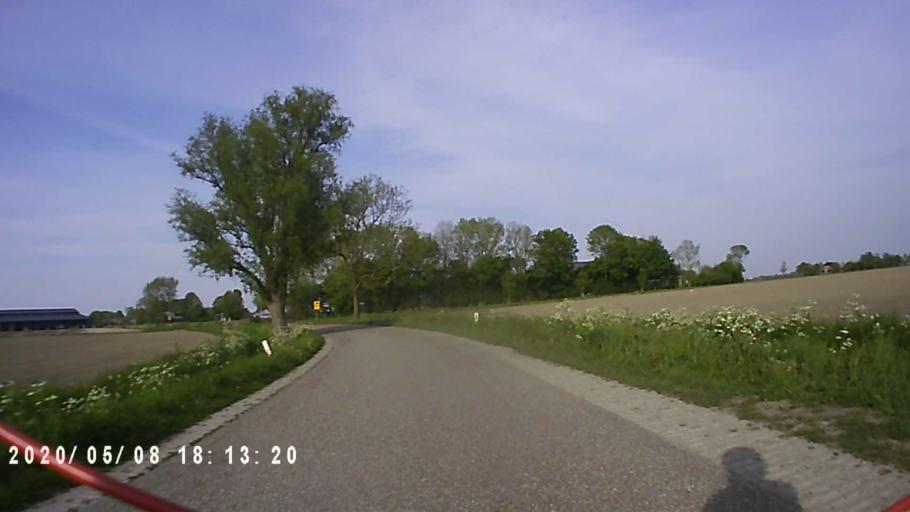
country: NL
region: Groningen
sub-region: Gemeente Winsum
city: Winsum
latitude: 53.3466
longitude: 6.4610
